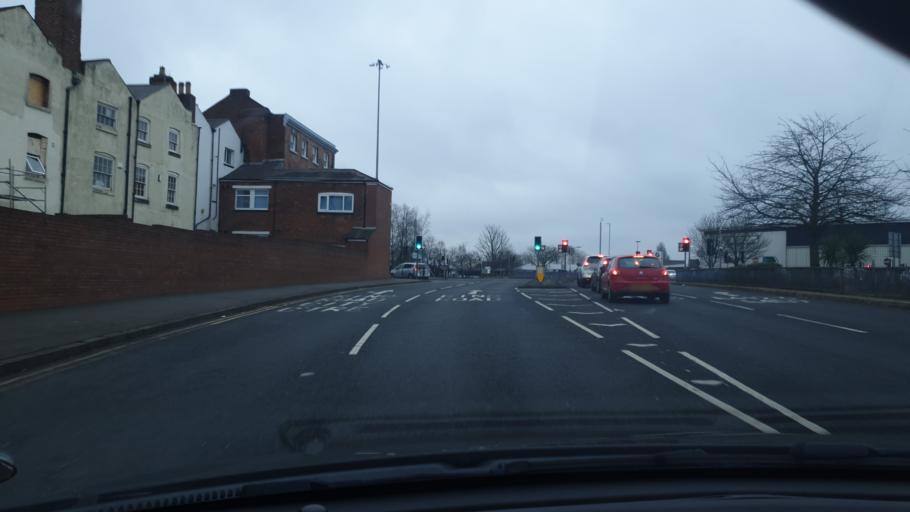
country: GB
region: England
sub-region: Wolverhampton
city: Wolverhampton
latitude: 52.5808
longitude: -2.1267
